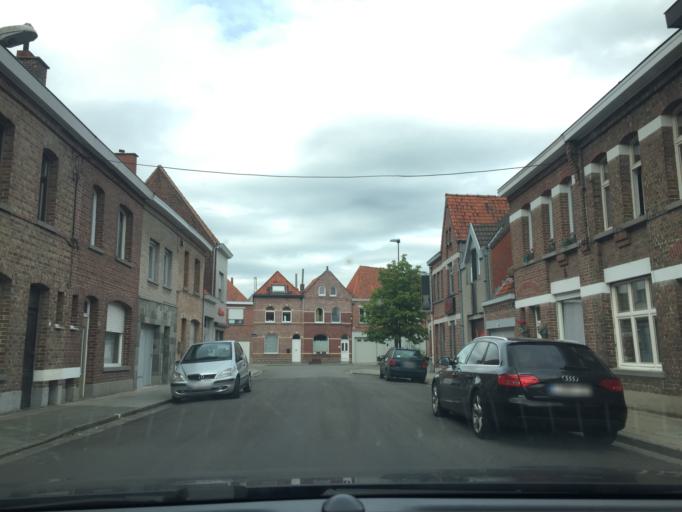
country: BE
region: Flanders
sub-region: Provincie West-Vlaanderen
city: Izegem
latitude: 50.9109
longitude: 3.2150
